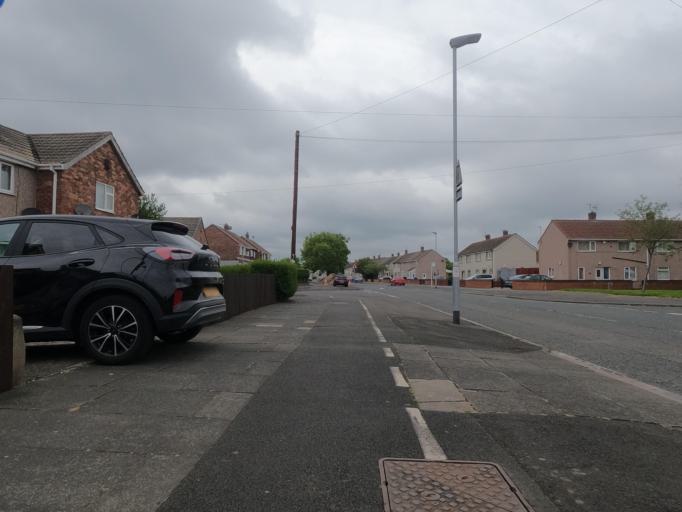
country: GB
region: England
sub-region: Northumberland
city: Blyth
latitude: 55.1223
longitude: -1.5388
